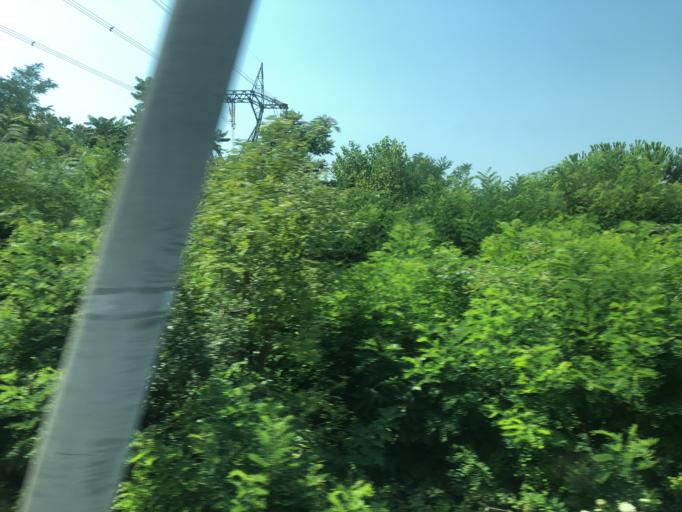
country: IT
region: Emilia-Romagna
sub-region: Provincia di Rimini
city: Santarcangelo
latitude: 44.0703
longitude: 12.4629
